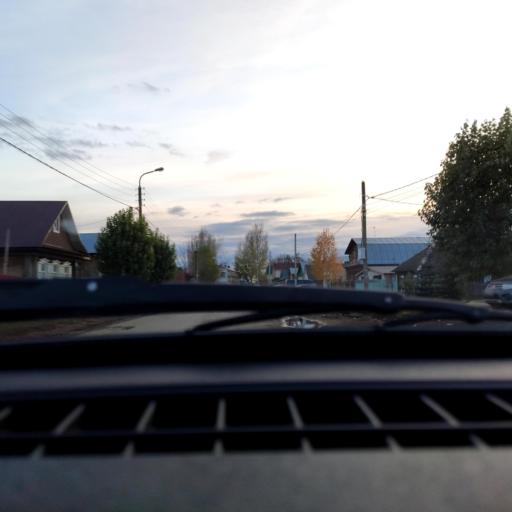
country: RU
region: Bashkortostan
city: Ufa
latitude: 54.7438
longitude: 55.9143
